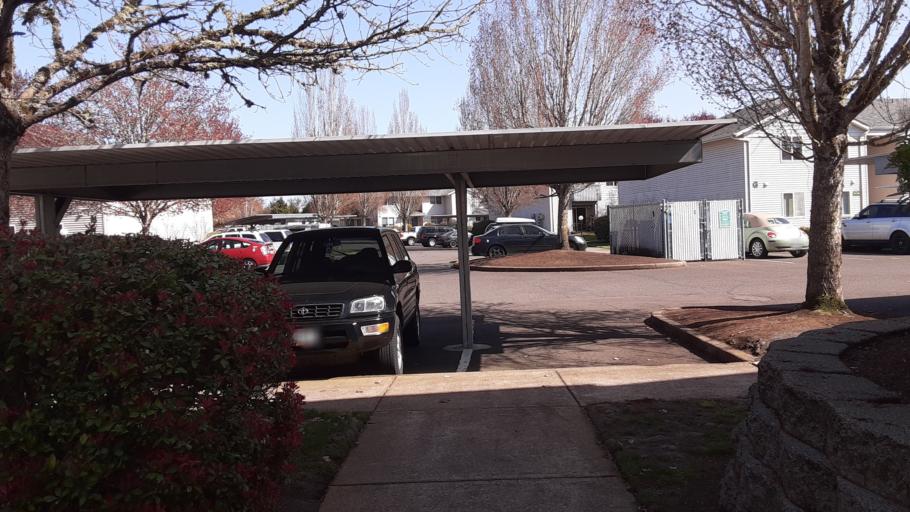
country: US
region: Oregon
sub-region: Benton County
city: Corvallis
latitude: 44.5336
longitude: -123.2581
